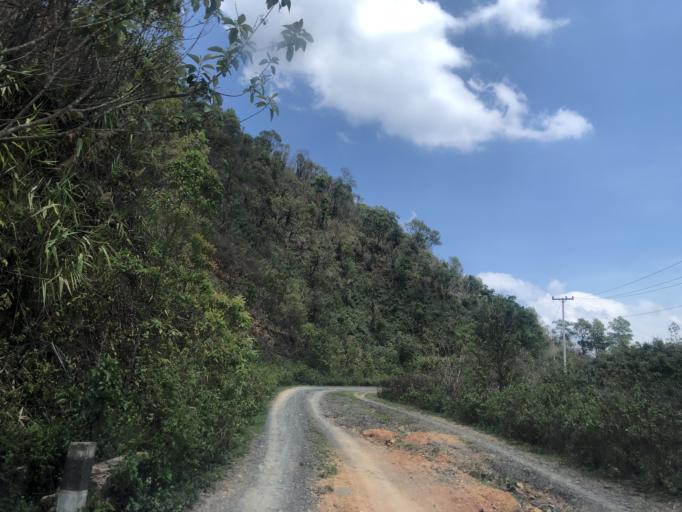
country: LA
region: Phongsali
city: Phongsali
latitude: 21.4349
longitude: 102.1612
